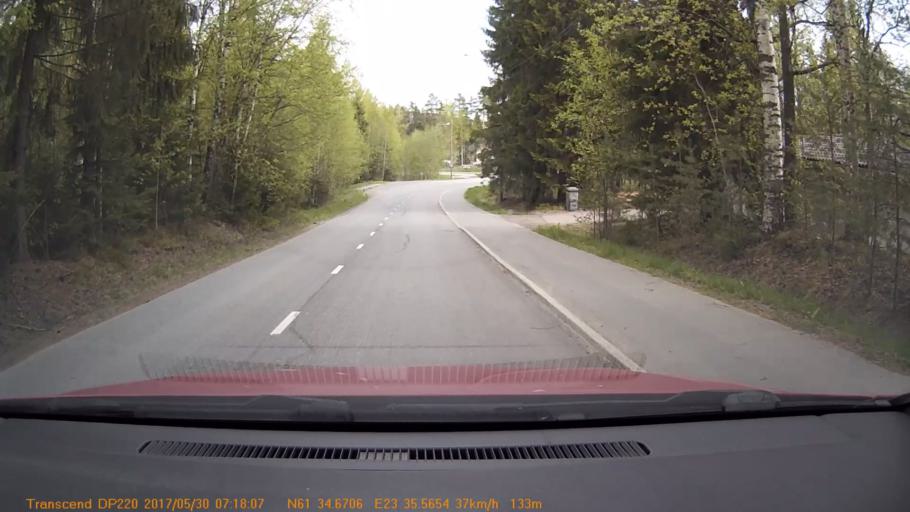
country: FI
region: Pirkanmaa
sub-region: Tampere
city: Yloejaervi
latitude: 61.5777
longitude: 23.5927
